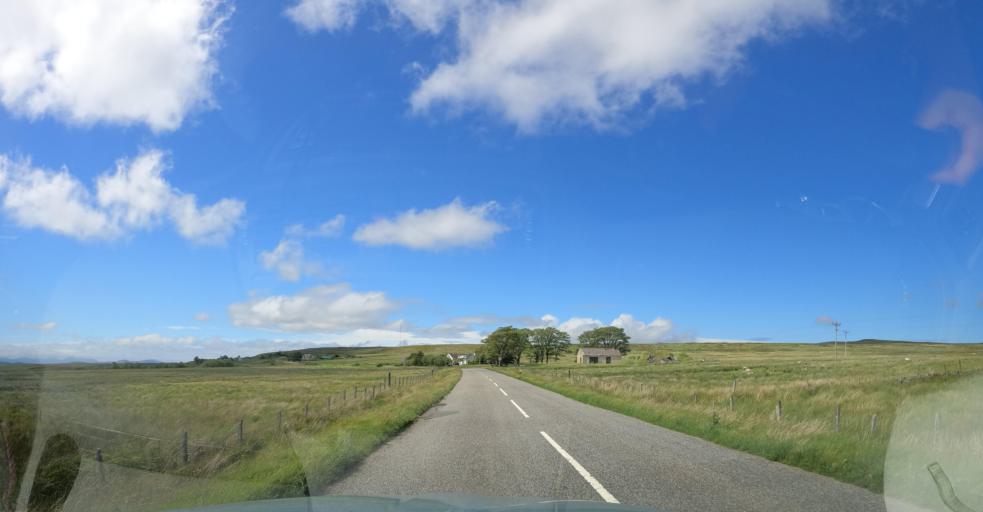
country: GB
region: Scotland
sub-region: Eilean Siar
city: Stornoway
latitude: 58.1638
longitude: -6.5400
